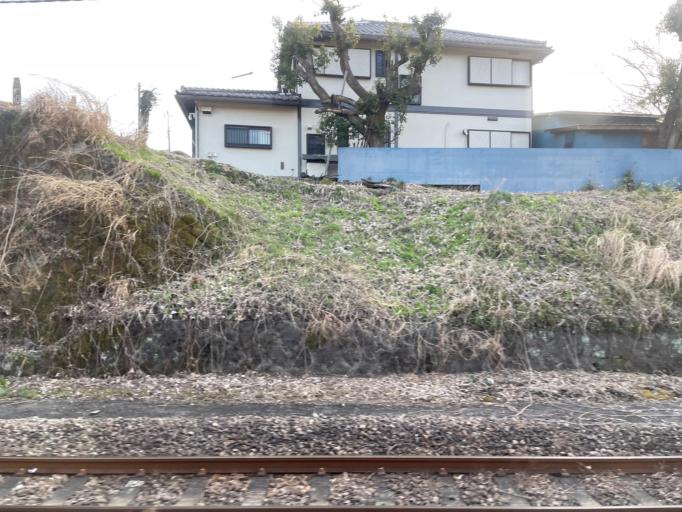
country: JP
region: Gunma
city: Annaka
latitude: 36.3105
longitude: 138.7957
